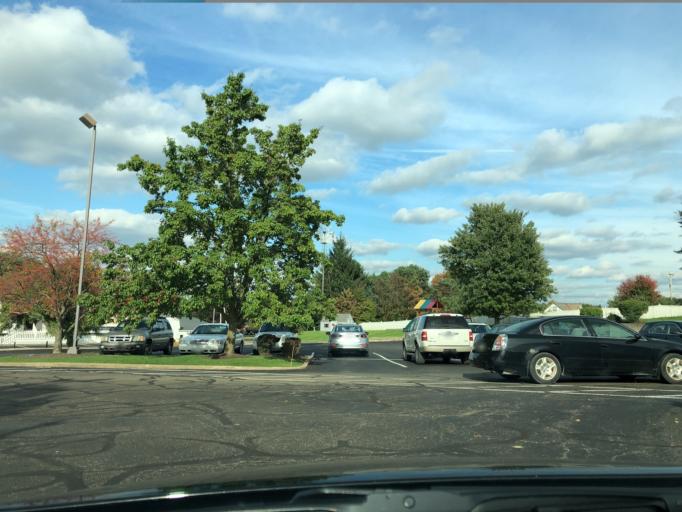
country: US
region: Ohio
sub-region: Stark County
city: Beach City
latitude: 40.6554
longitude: -81.6389
